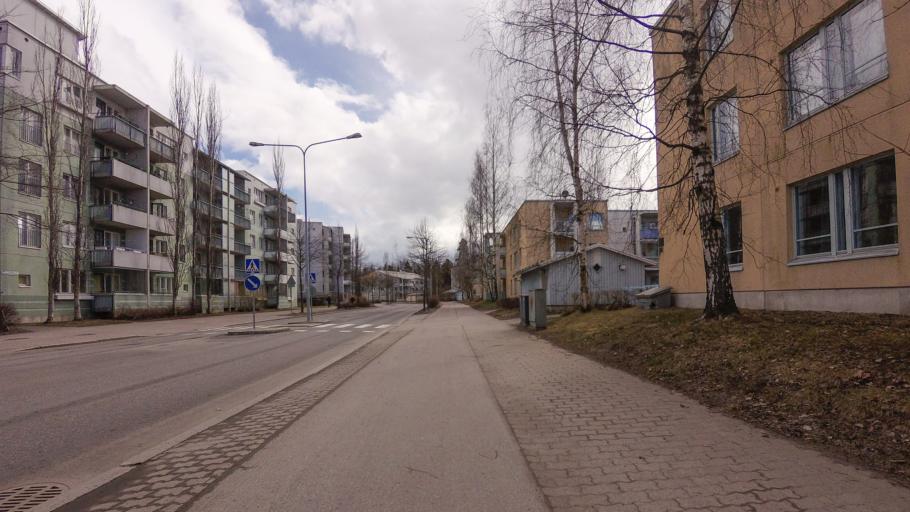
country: FI
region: Uusimaa
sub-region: Helsinki
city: Vantaa
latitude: 60.2021
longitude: 25.1170
